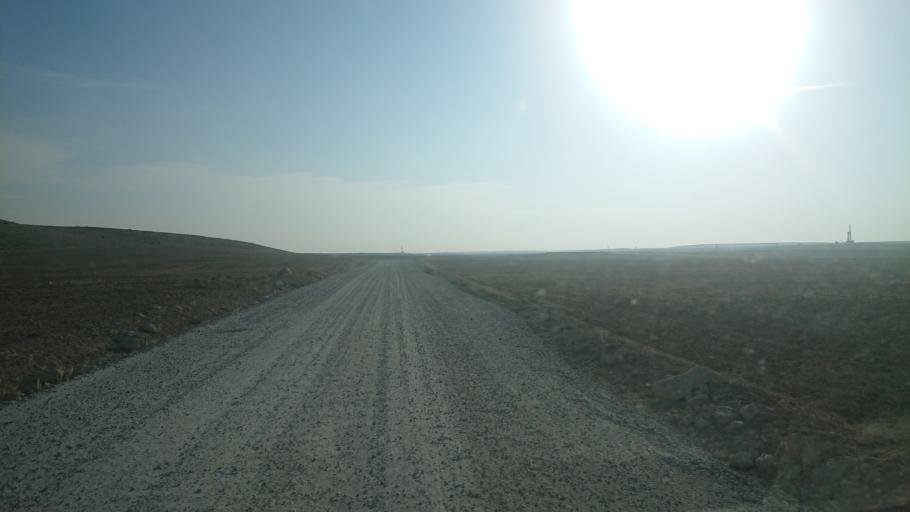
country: TR
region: Aksaray
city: Sultanhani
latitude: 38.0849
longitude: 33.6211
